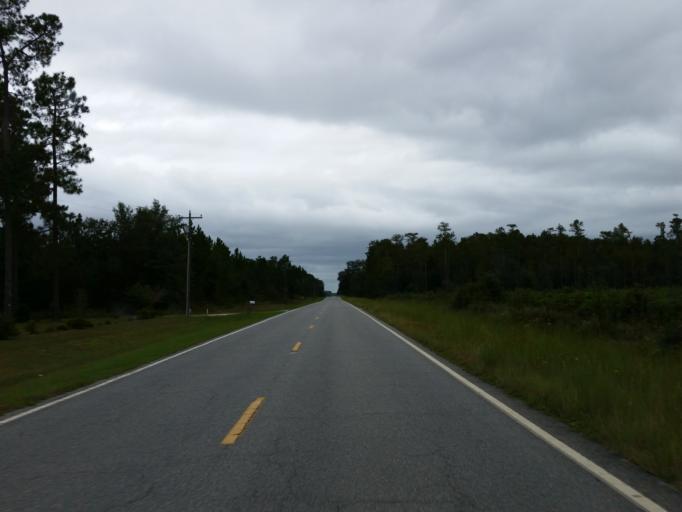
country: US
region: Georgia
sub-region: Echols County
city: Statenville
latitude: 30.8751
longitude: -83.0019
